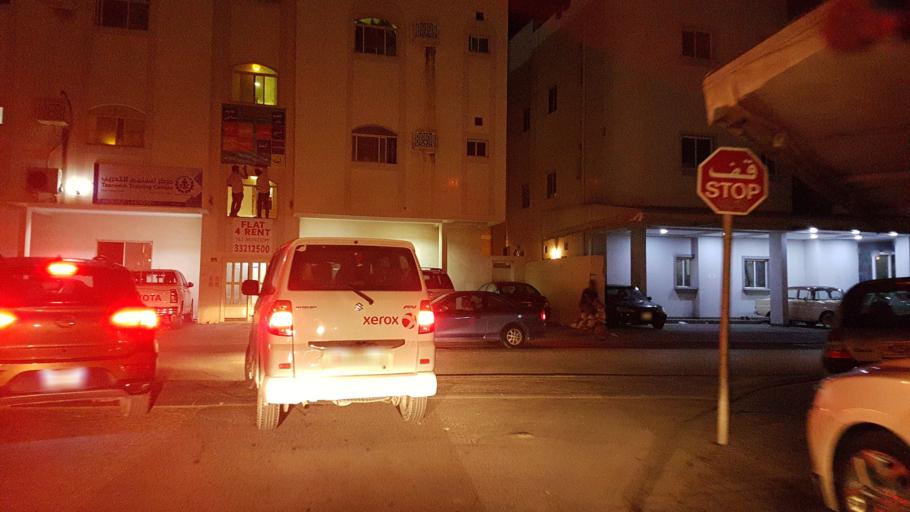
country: BH
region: Manama
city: Jidd Hafs
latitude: 26.2211
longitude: 50.5115
